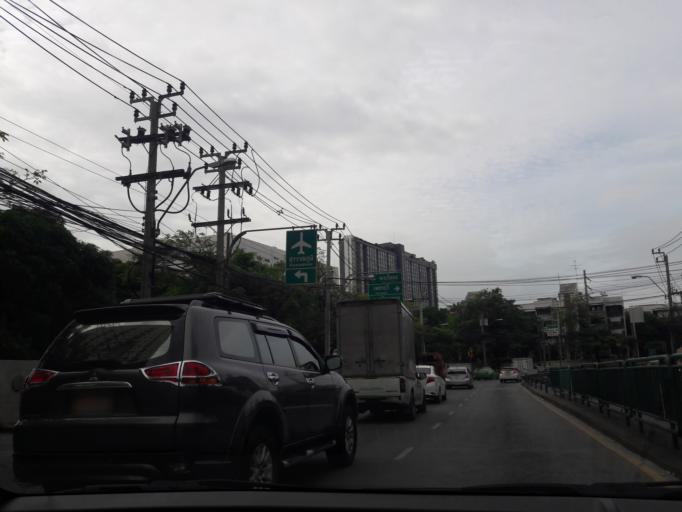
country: TH
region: Bangkok
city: Watthana
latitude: 13.7423
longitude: 100.6015
